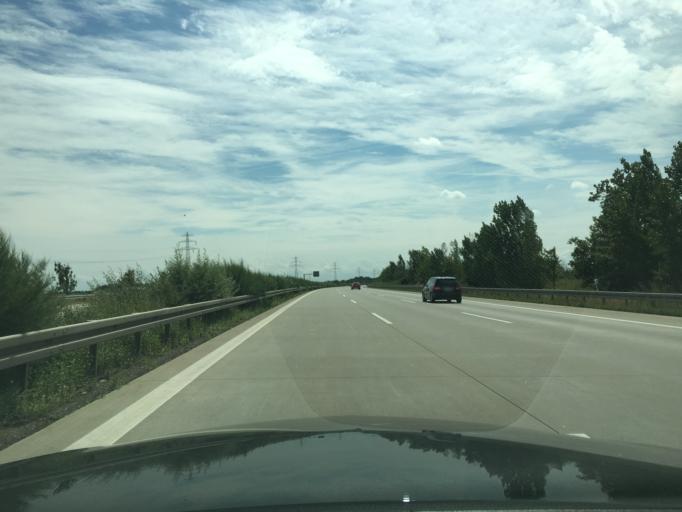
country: DE
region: Saxony-Anhalt
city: Brehna
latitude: 51.5349
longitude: 12.1956
